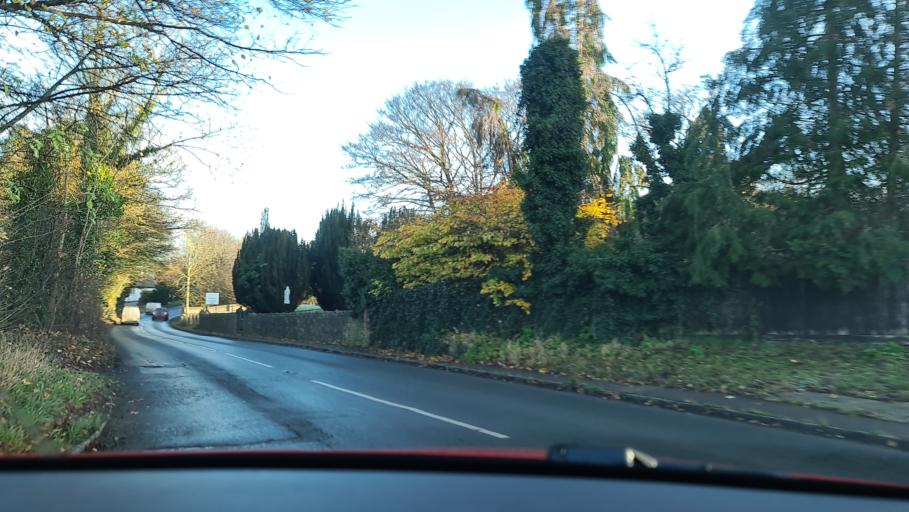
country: GB
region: England
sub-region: Buckinghamshire
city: Princes Risborough
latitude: 51.7503
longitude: -0.8048
